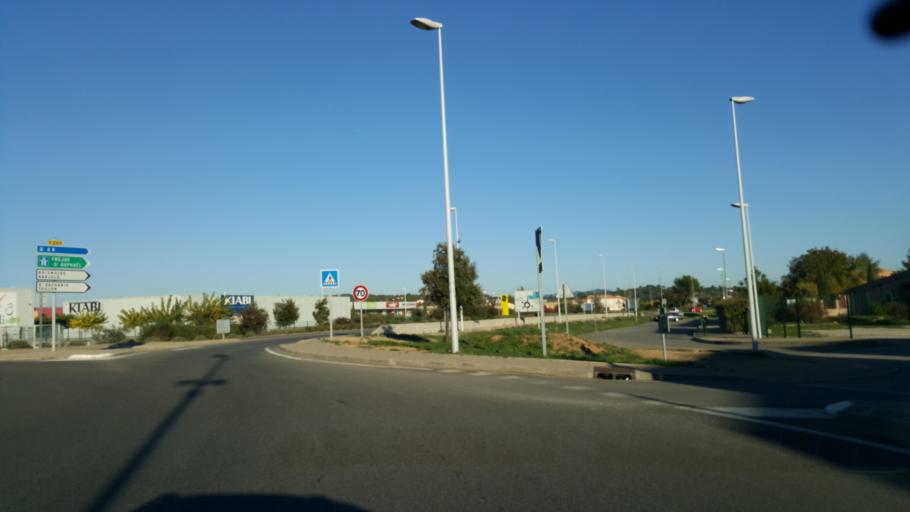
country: FR
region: Provence-Alpes-Cote d'Azur
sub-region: Departement du Var
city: Saint-Maximin-la-Sainte-Baume
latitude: 43.4587
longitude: 5.8598
